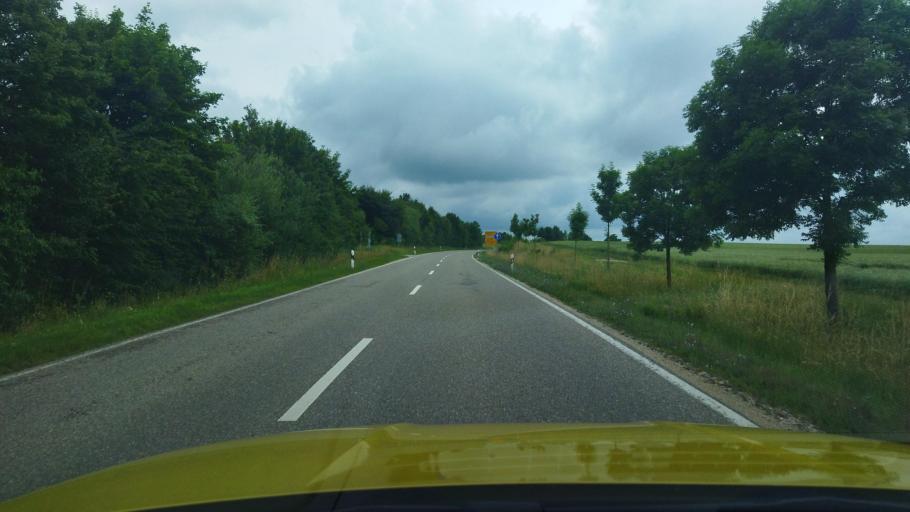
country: DE
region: Bavaria
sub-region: Regierungsbezirk Mittelfranken
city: Ettenstatt
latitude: 49.0829
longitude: 11.0557
